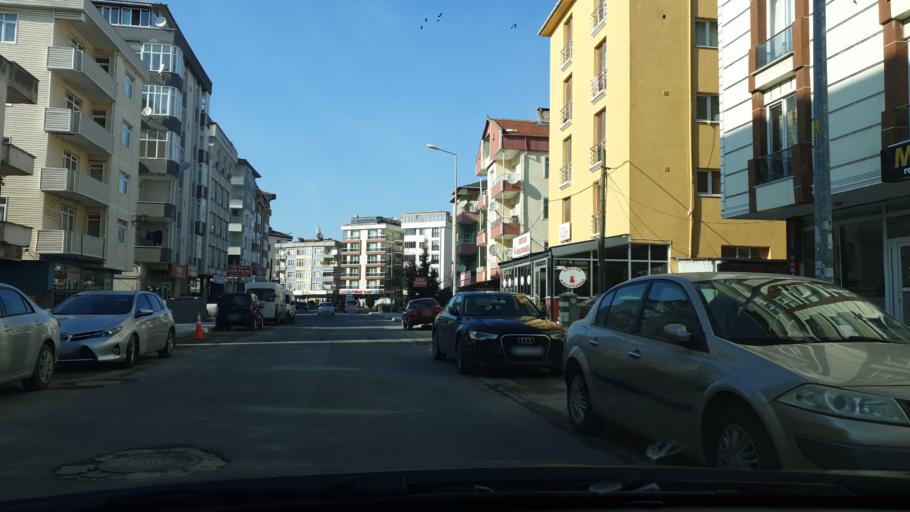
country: TR
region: Tekirdag
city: Cerkezkoey
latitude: 41.2867
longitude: 27.9930
